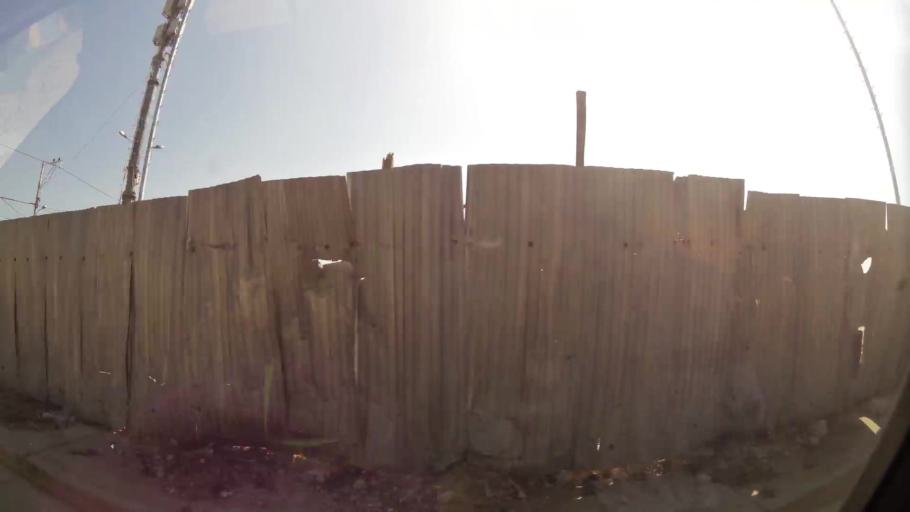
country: CO
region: Bolivar
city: Cartagena
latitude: 10.4137
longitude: -75.5102
